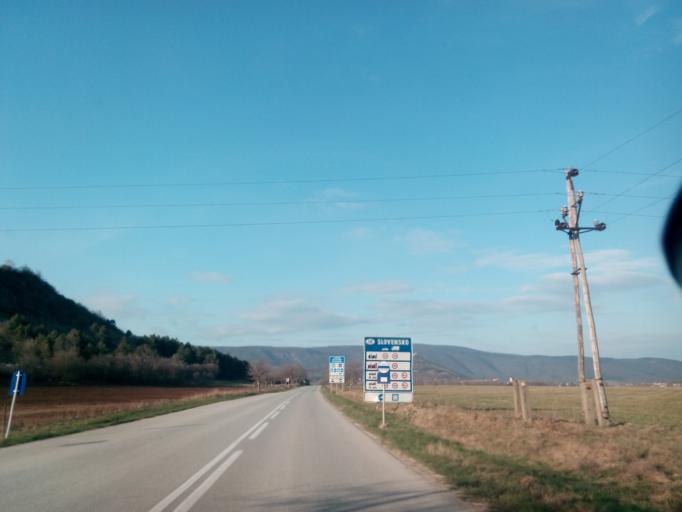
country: SK
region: Kosicky
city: Medzev
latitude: 48.5820
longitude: 20.8507
